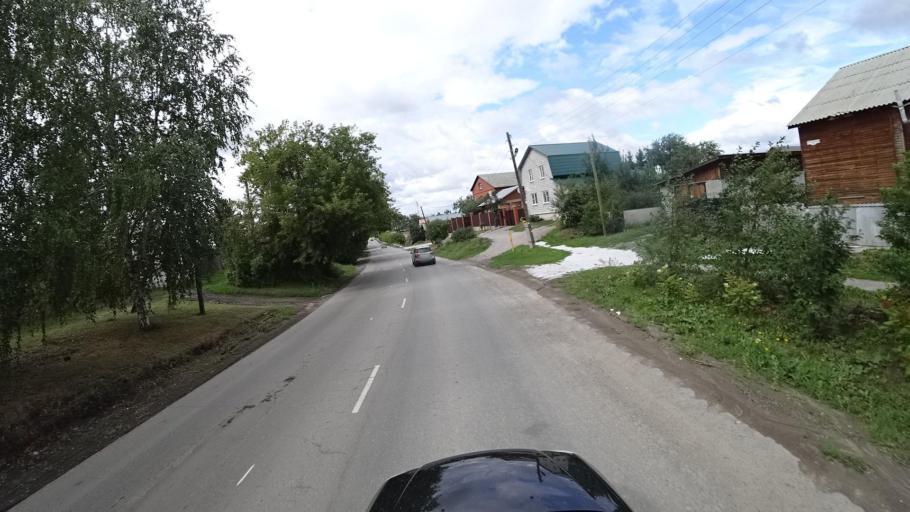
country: RU
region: Sverdlovsk
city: Kamyshlov
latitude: 56.8535
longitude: 62.7083
